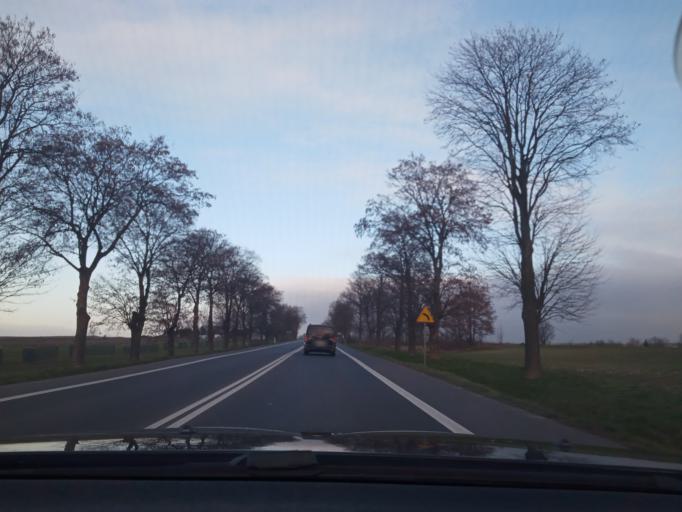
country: PL
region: Lesser Poland Voivodeship
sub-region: Powiat krakowski
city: Slomniki
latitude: 50.2718
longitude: 20.0692
